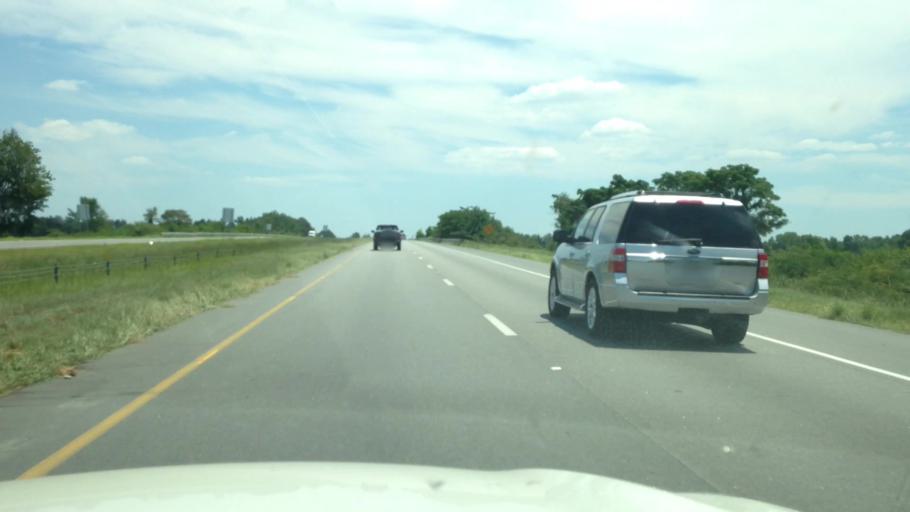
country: US
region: South Carolina
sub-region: Lee County
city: Bishopville
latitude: 34.1916
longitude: -80.2615
